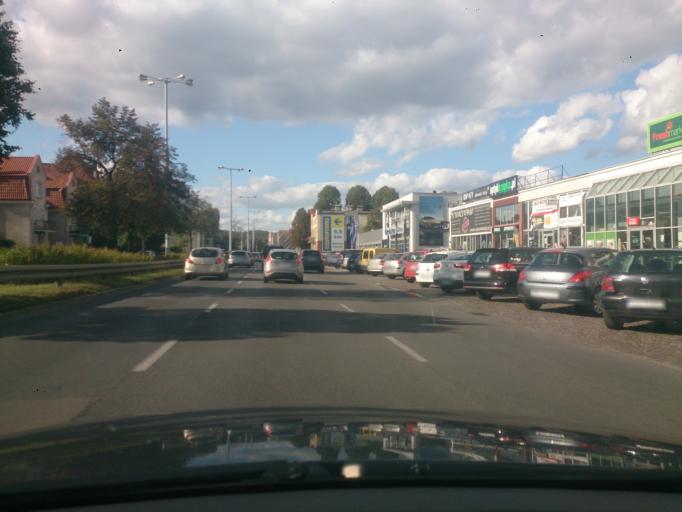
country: PL
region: Pomeranian Voivodeship
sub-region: Sopot
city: Sopot
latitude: 54.4069
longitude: 18.5701
